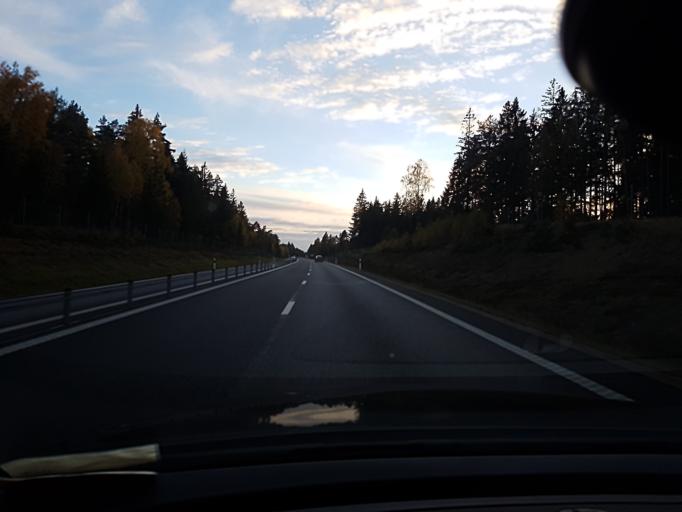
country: SE
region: Kronoberg
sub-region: Ljungby Kommun
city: Ljungby
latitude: 56.7820
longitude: 13.8213
